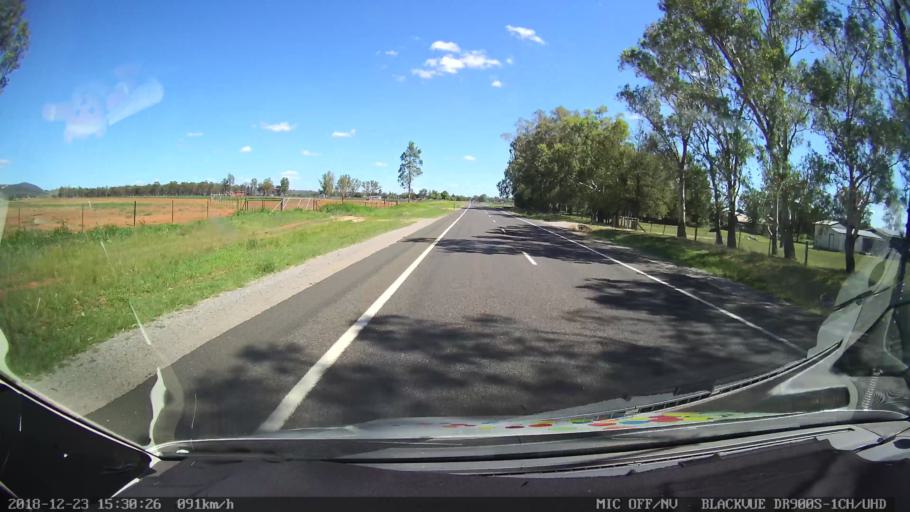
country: AU
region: New South Wales
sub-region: Tamworth Municipality
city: East Tamworth
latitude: -30.9587
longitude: 150.8663
